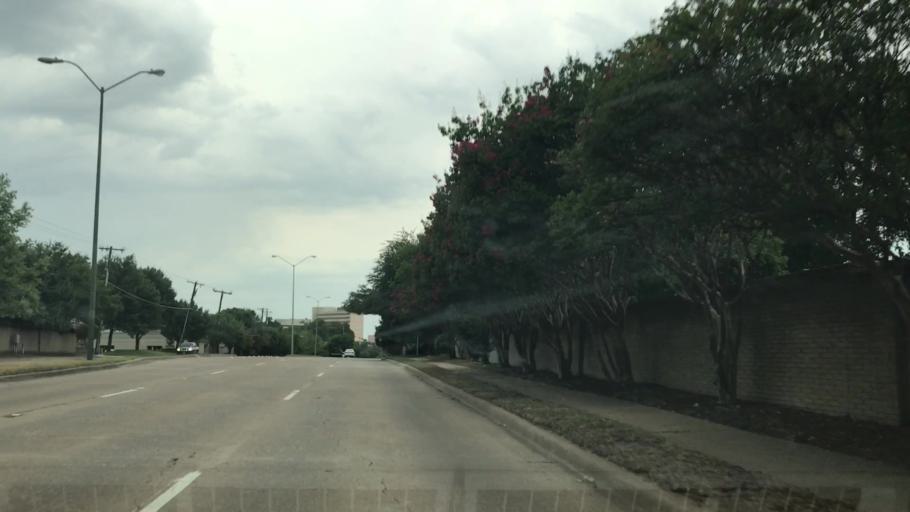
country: US
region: Texas
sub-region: Dallas County
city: Addison
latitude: 32.9500
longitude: -96.7947
